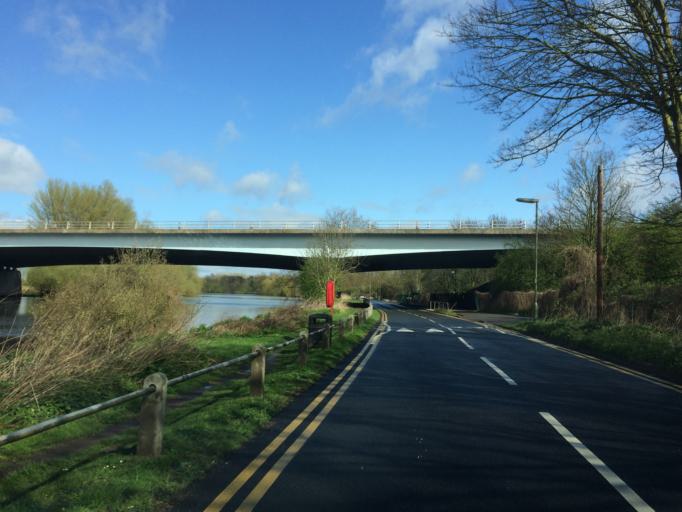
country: GB
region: England
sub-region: Surrey
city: Chertsey
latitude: 51.3933
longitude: -0.4859
